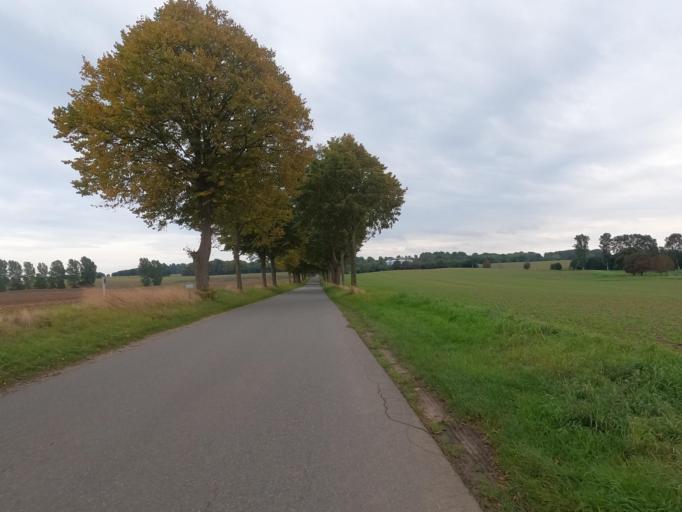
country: DE
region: Schleswig-Holstein
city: Neukirchen
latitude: 54.2982
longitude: 11.0504
